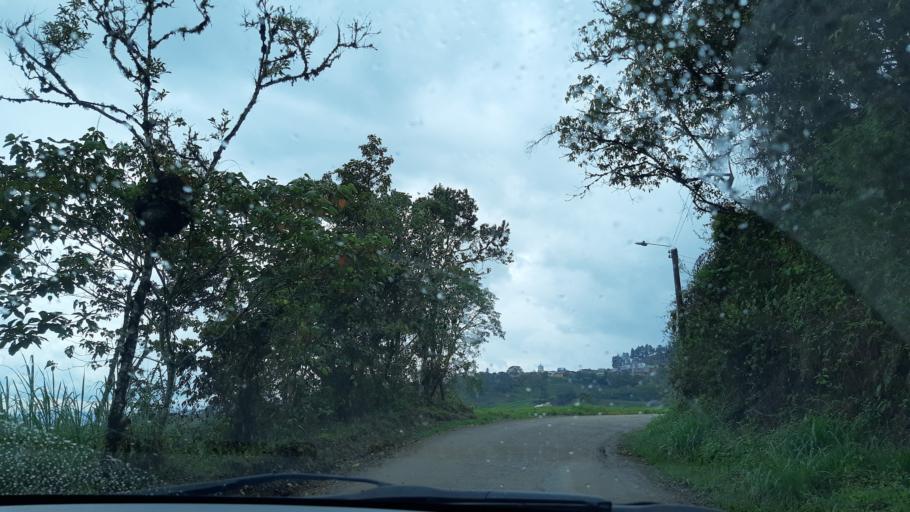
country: CO
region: Boyaca
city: Chivor
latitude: 4.9654
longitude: -73.3160
